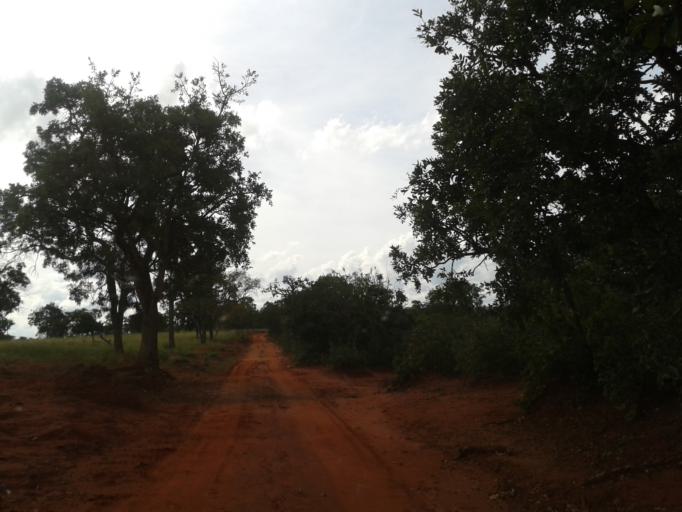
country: BR
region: Minas Gerais
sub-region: Campina Verde
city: Campina Verde
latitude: -19.4410
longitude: -49.6178
